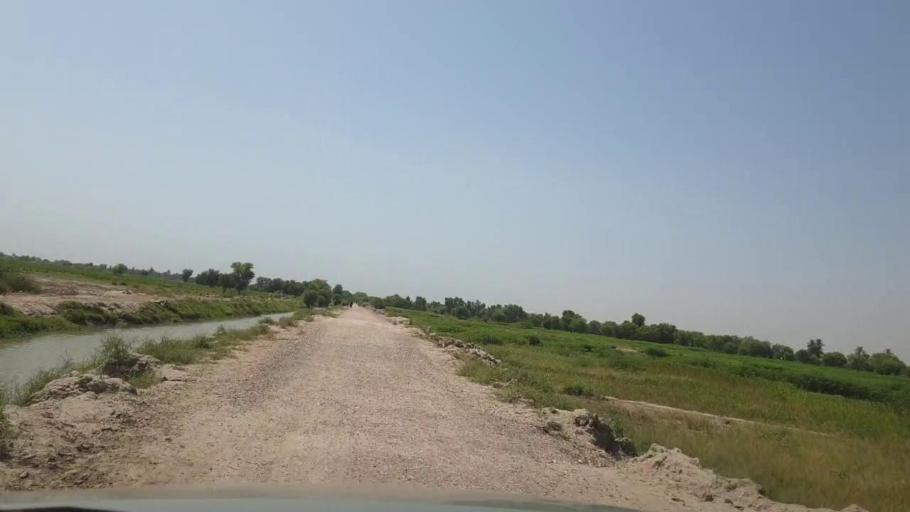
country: PK
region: Sindh
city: Rohri
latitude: 27.6603
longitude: 68.9815
